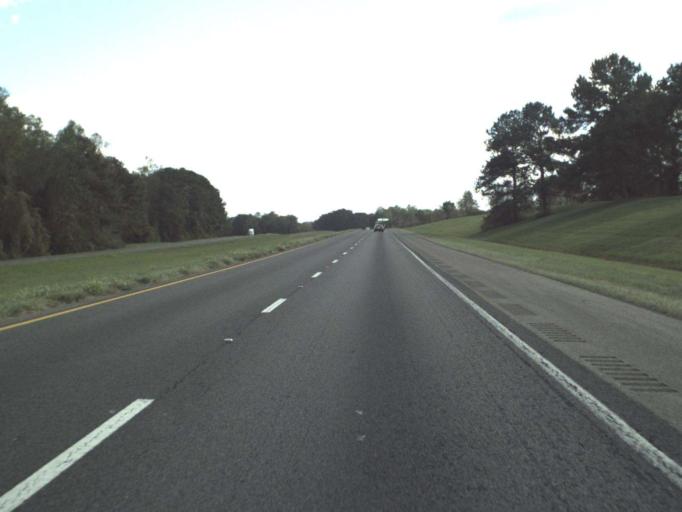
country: US
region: Florida
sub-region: Gadsden County
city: Gretna
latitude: 30.5928
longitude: -84.7220
